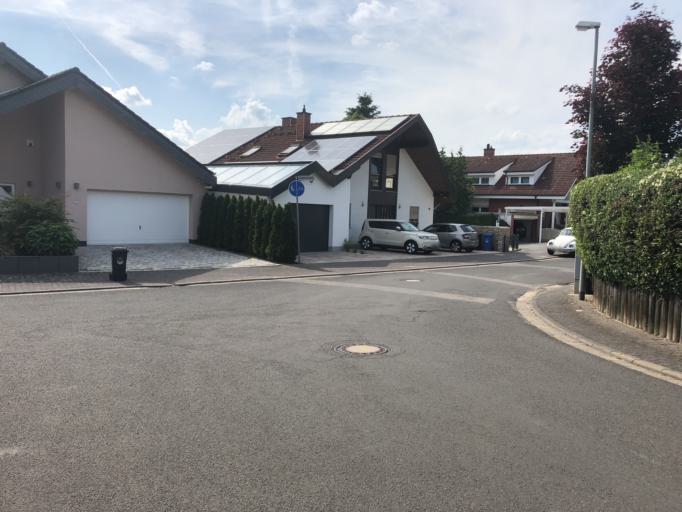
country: DE
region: Hesse
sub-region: Regierungsbezirk Darmstadt
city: Konigstein im Taunus
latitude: 50.1747
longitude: 8.4633
